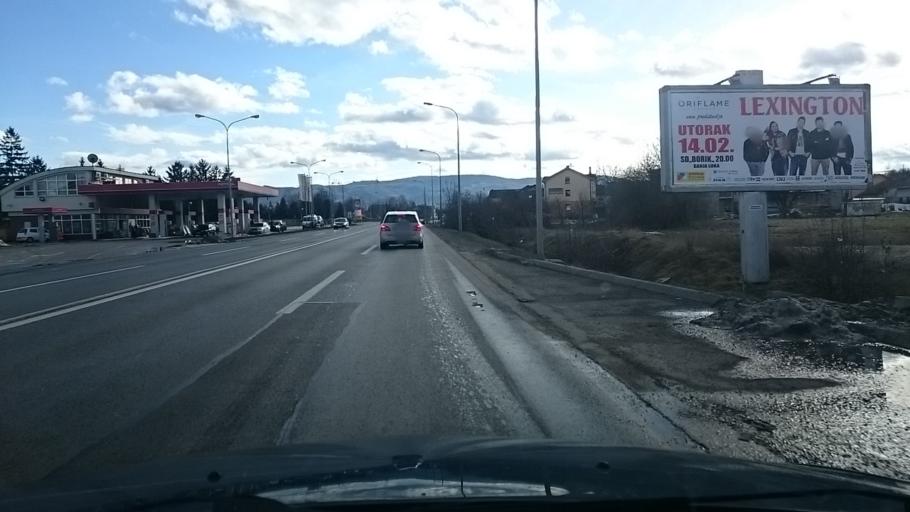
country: BA
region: Republika Srpska
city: Banja Luka
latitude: 44.8042
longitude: 17.1983
